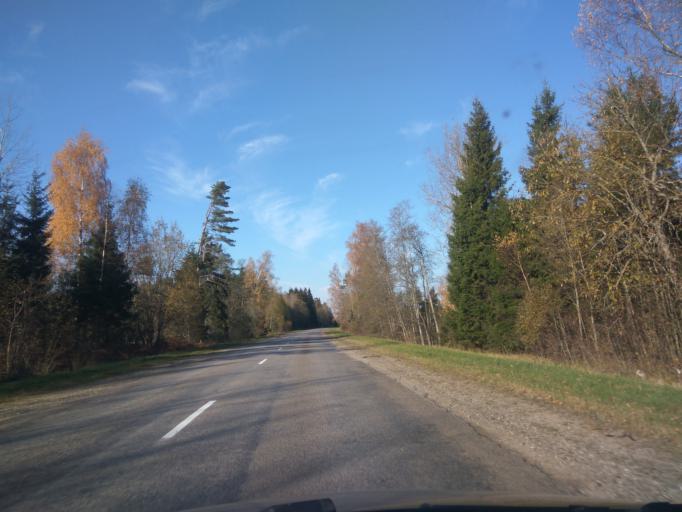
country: LV
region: Kuldigas Rajons
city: Kuldiga
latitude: 57.0444
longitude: 21.8265
